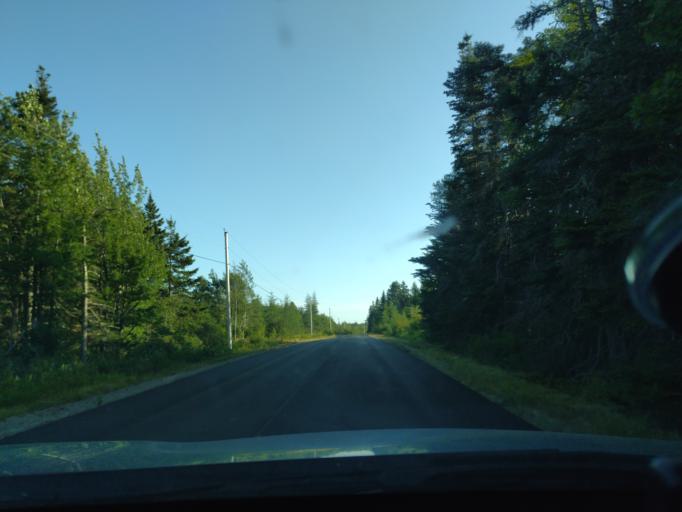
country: US
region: Maine
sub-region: Washington County
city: Machiasport
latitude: 44.6917
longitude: -67.1653
